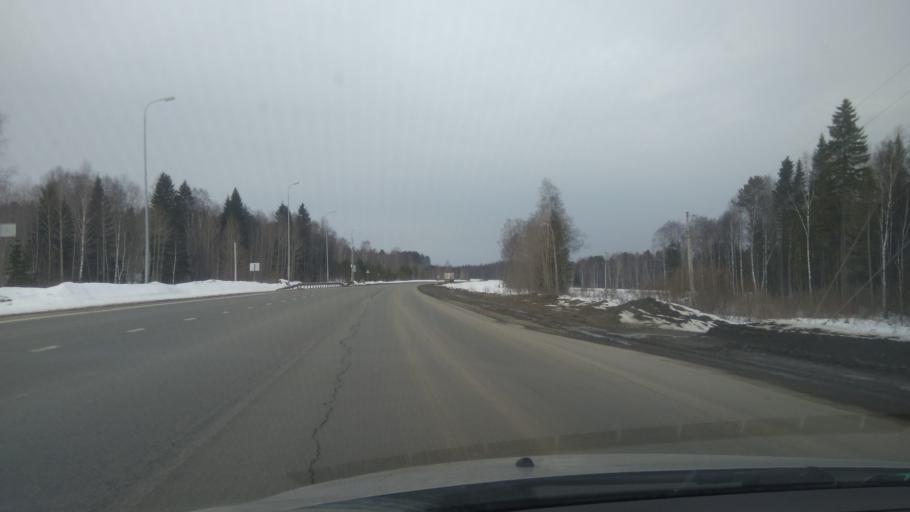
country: RU
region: Sverdlovsk
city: Ufimskiy
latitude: 56.7820
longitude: 58.4007
